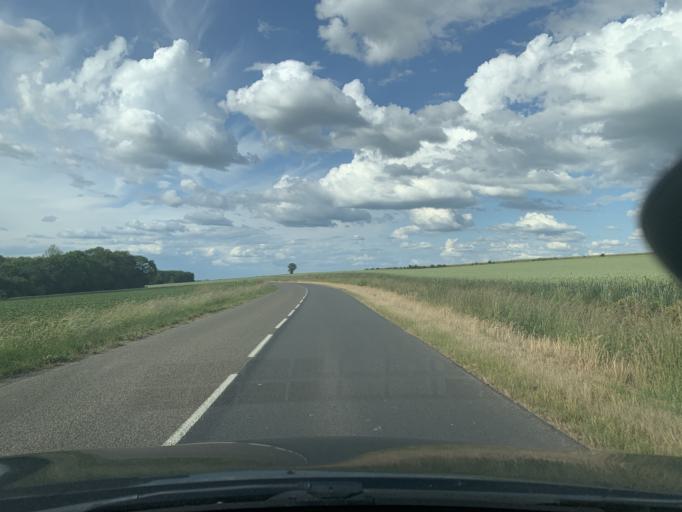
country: FR
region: Nord-Pas-de-Calais
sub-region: Departement du Nord
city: Marcoing
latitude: 50.0937
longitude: 3.1512
